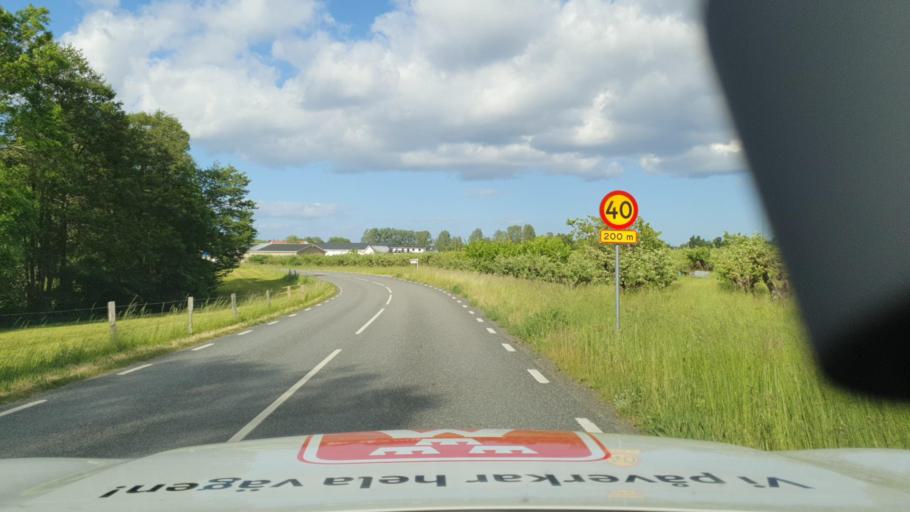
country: SE
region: Skane
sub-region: Simrishamns Kommun
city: Kivik
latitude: 55.6231
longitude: 14.2487
